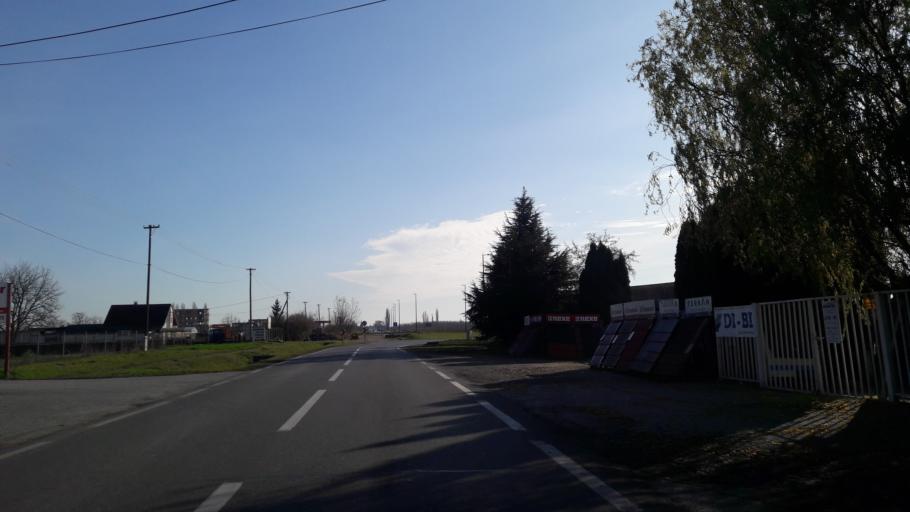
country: HR
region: Osjecko-Baranjska
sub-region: Grad Osijek
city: Osijek
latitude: 45.5383
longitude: 18.7143
